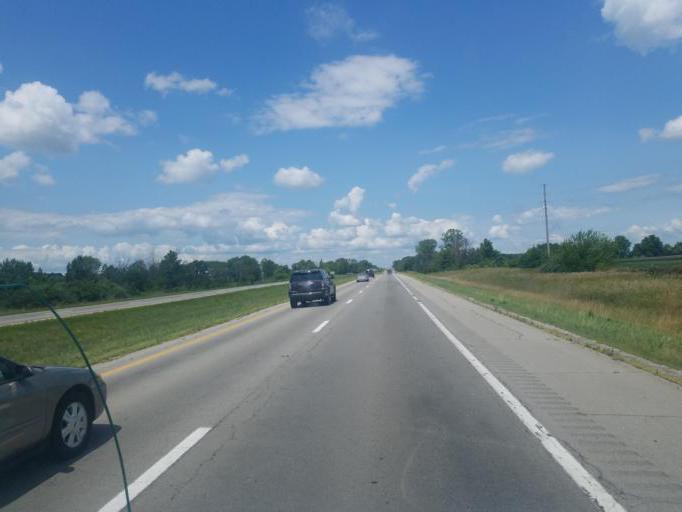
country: US
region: Ohio
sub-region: Marion County
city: Marion
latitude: 40.5415
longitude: -83.0744
